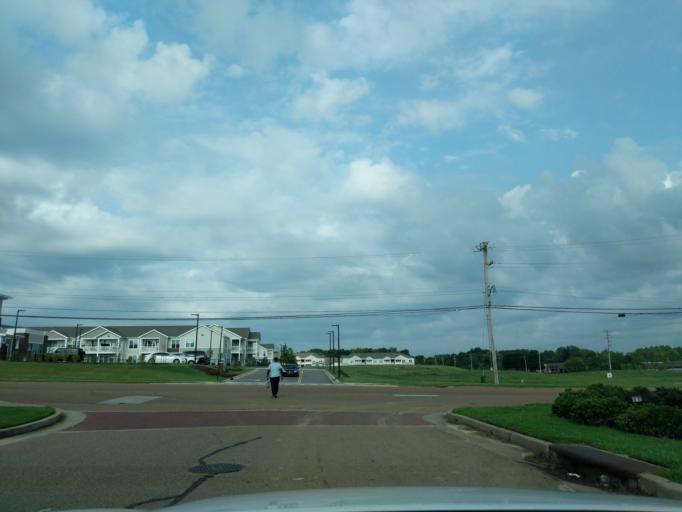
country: US
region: Tennessee
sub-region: Shelby County
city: Germantown
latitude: 35.0467
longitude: -89.7594
